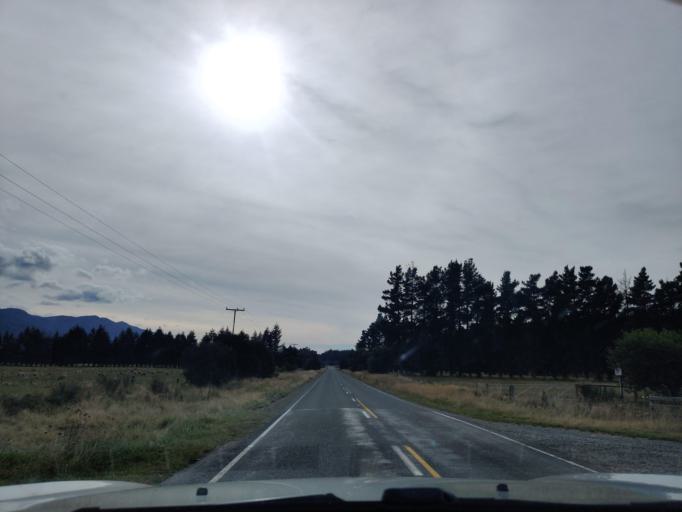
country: NZ
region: Tasman
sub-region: Tasman District
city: Brightwater
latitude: -41.6669
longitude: 173.1979
